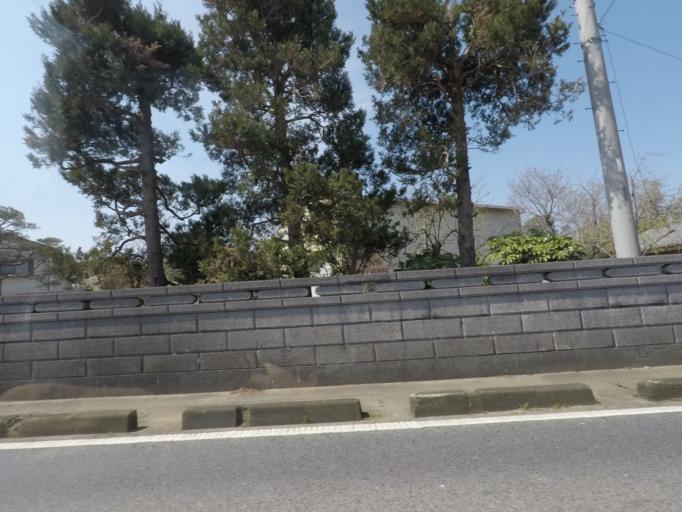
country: JP
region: Chiba
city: Narita
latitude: 35.7691
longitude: 140.3534
